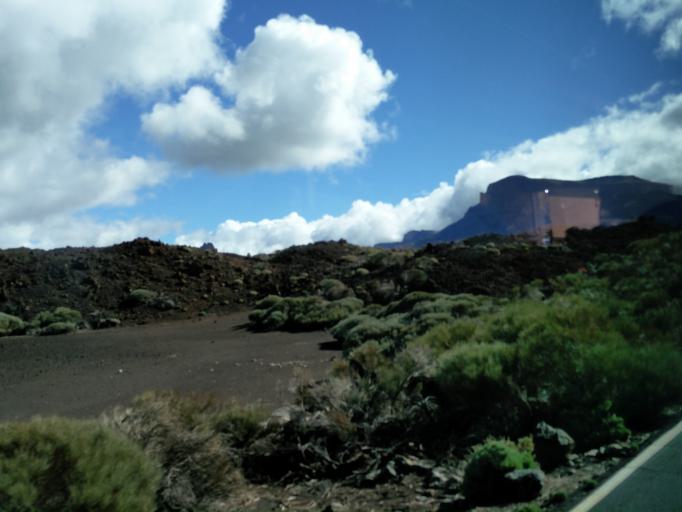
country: ES
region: Canary Islands
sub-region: Provincia de Santa Cruz de Tenerife
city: Vilaflor
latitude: 28.2141
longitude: -16.6644
